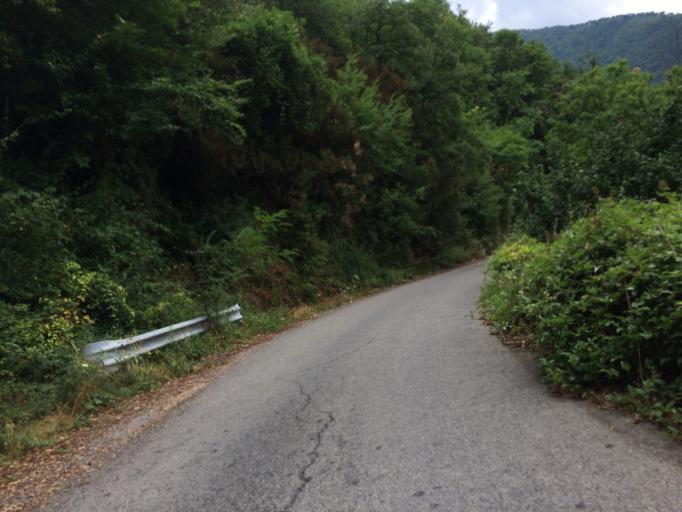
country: IT
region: Liguria
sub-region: Provincia di Imperia
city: Castel Vittorio
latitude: 43.9406
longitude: 7.6871
